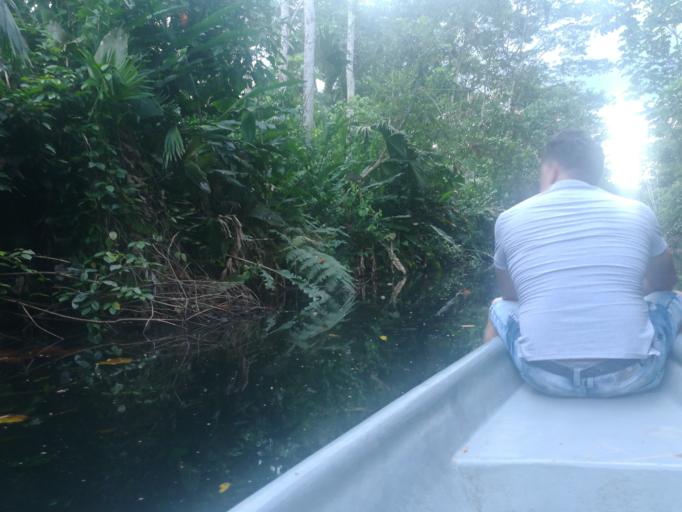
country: EC
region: Napo
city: Tena
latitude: -1.0407
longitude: -77.6651
